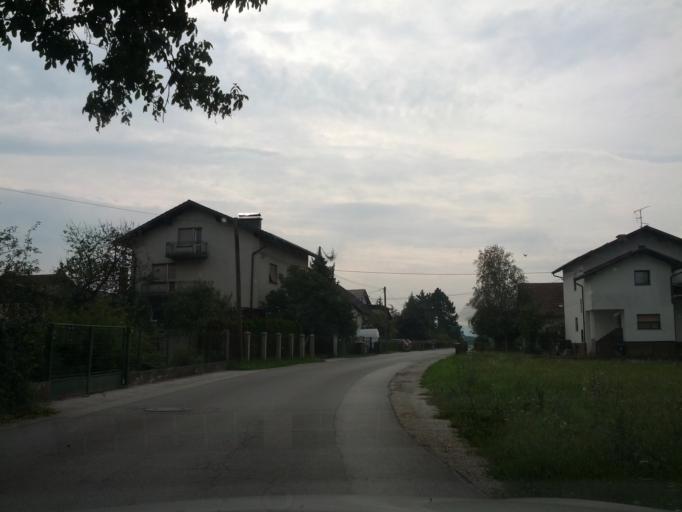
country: SI
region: Dol pri Ljubljani
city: Dol pri Ljubljani
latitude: 46.0753
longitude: 14.5608
